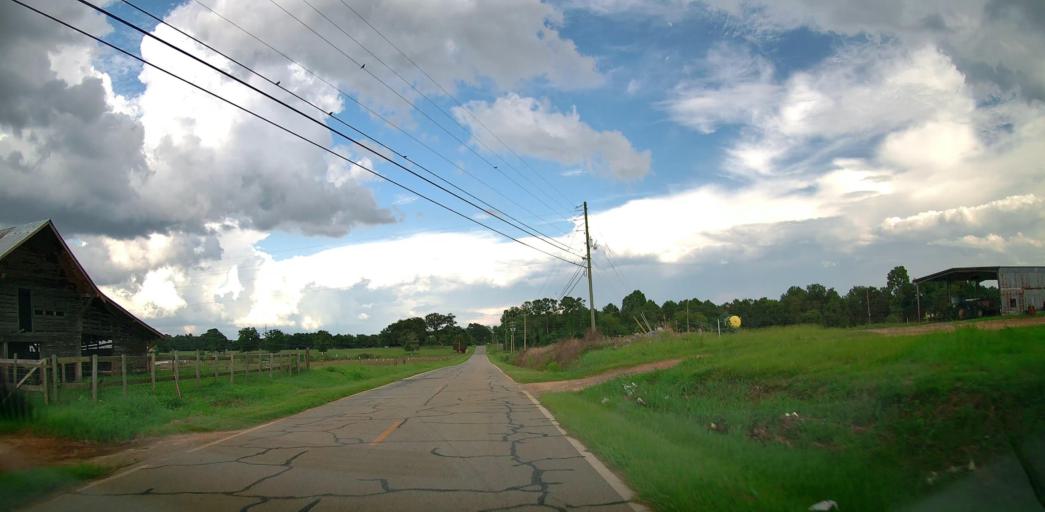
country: US
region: Georgia
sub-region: Bleckley County
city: Cochran
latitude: 32.3959
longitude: -83.3690
